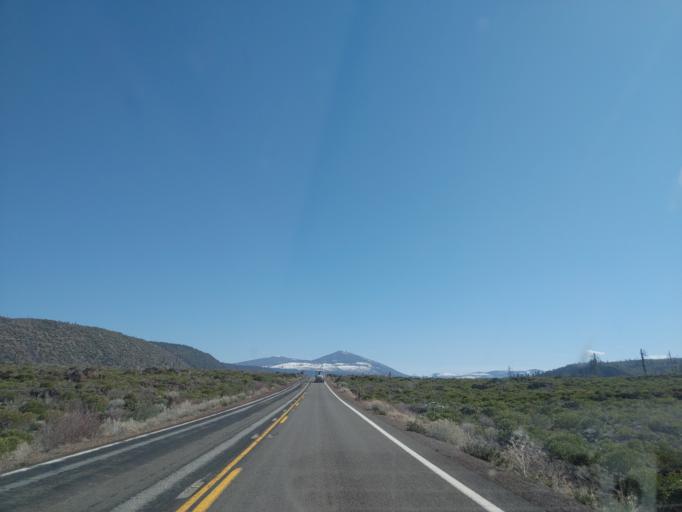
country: US
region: California
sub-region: Shasta County
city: Burney
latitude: 40.7174
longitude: -121.4238
